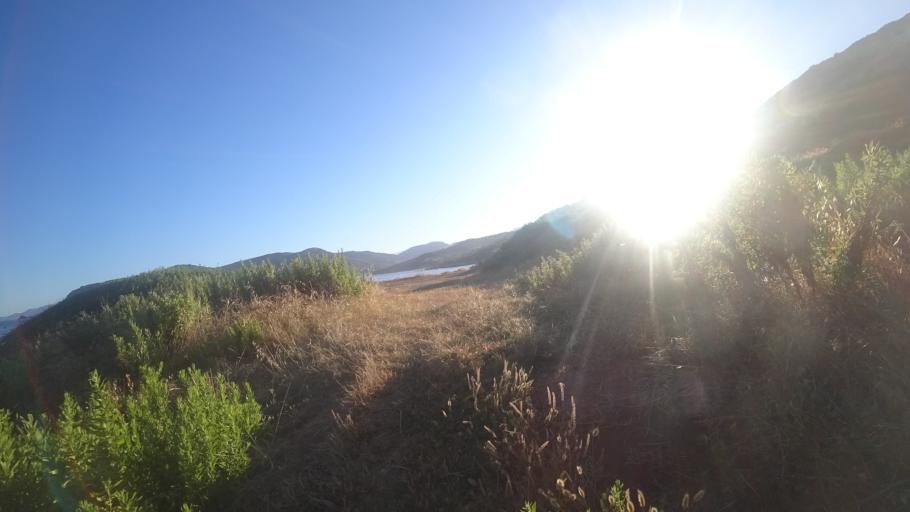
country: FR
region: Corsica
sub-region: Departement de la Corse-du-Sud
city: Alata
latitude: 41.9759
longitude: 8.6611
